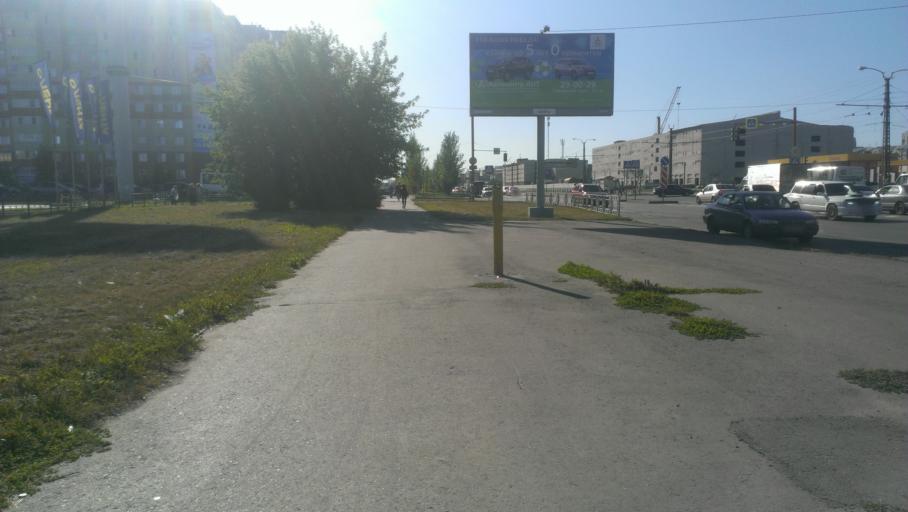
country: RU
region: Altai Krai
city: Novosilikatnyy
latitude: 53.3277
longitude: 83.6850
